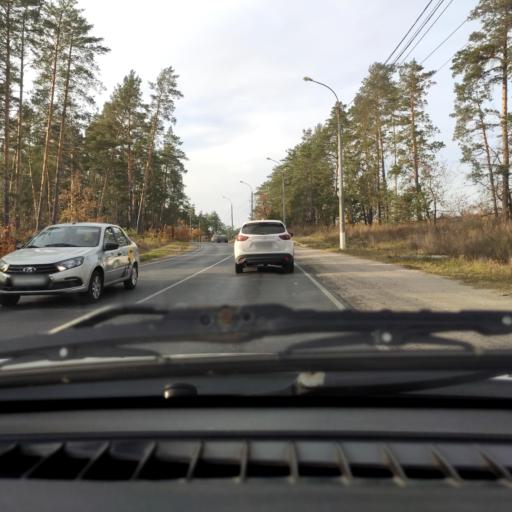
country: RU
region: Samara
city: Tol'yatti
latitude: 53.4819
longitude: 49.3208
